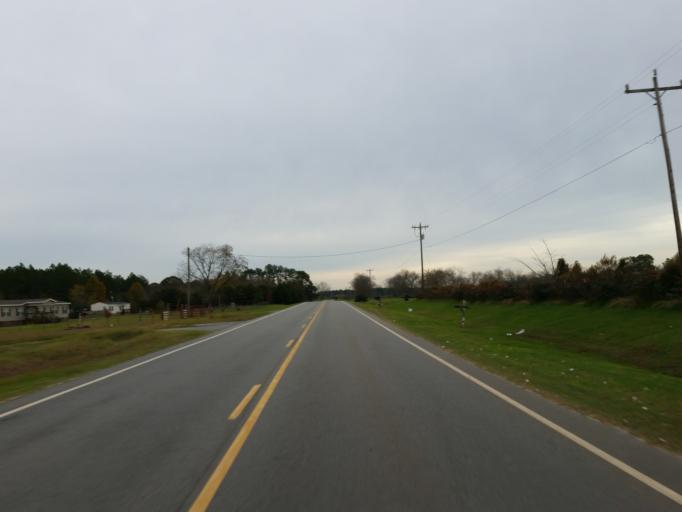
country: US
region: Georgia
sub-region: Turner County
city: Ashburn
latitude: 31.6665
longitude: -83.6256
